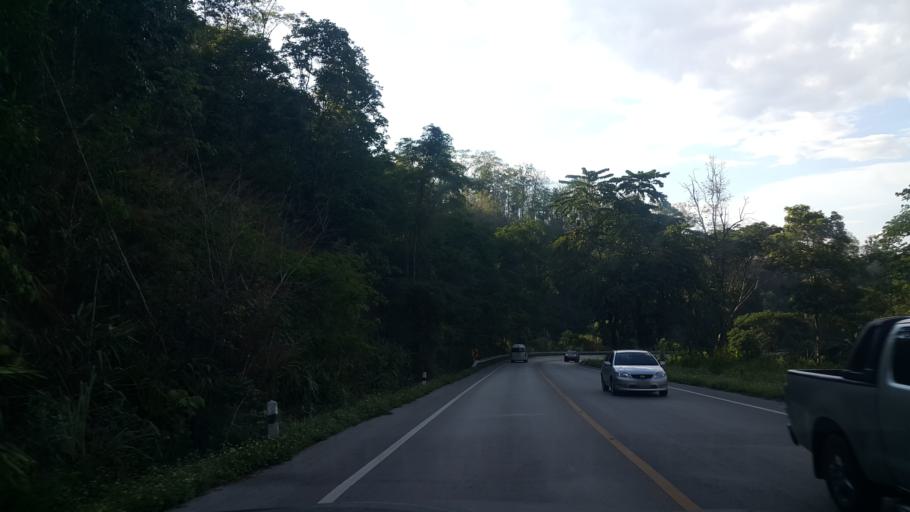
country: TH
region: Lampang
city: Wang Nuea
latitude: 19.0639
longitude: 99.7288
